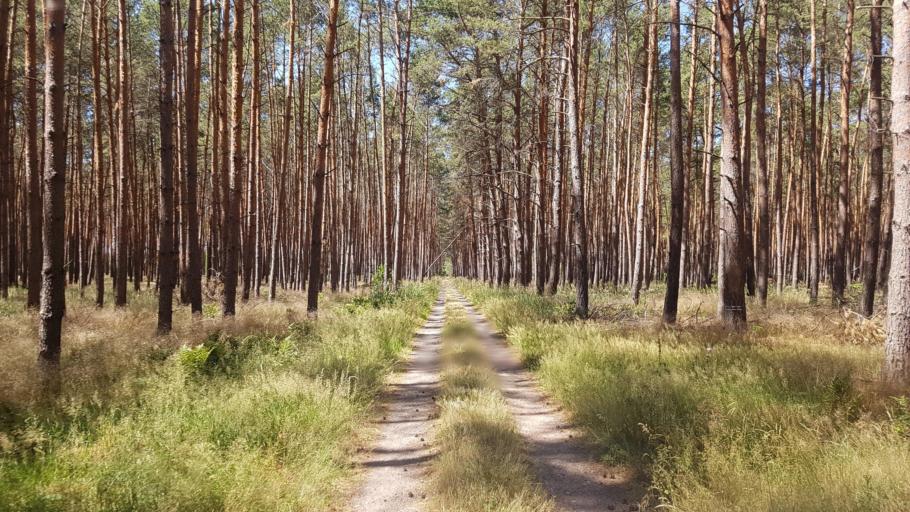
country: DE
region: Brandenburg
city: Treuenbrietzen
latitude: 52.0451
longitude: 12.8475
